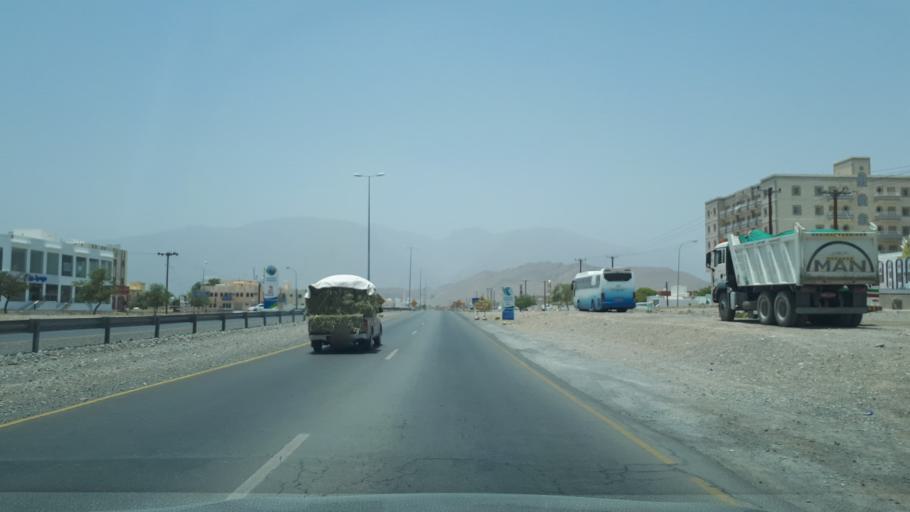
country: OM
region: Al Batinah
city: Rustaq
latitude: 23.4496
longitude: 57.4329
